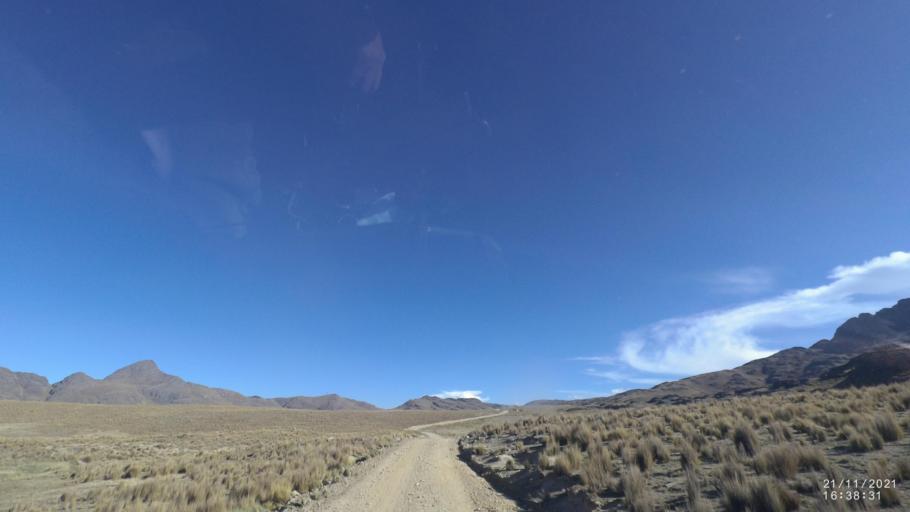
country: BO
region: Cochabamba
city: Cochabamba
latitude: -17.0516
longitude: -66.2621
